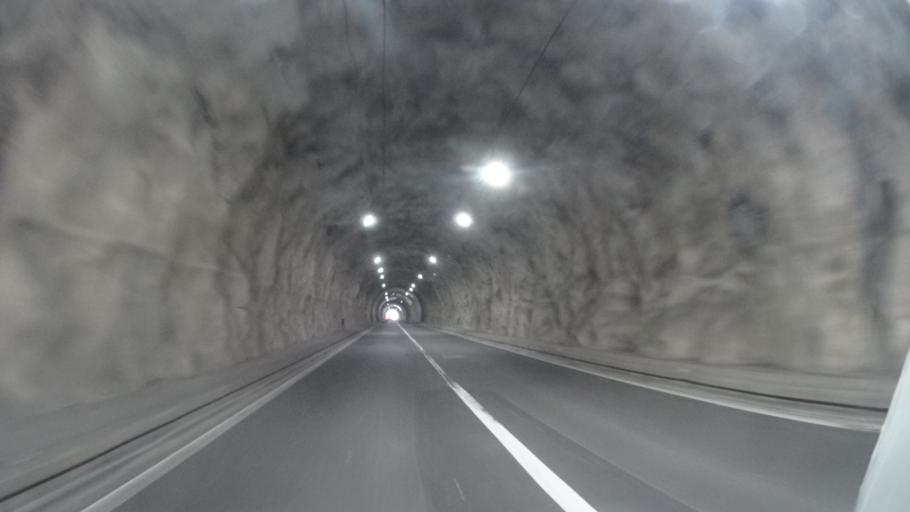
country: JP
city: Asahi
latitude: 35.9650
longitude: 135.9696
